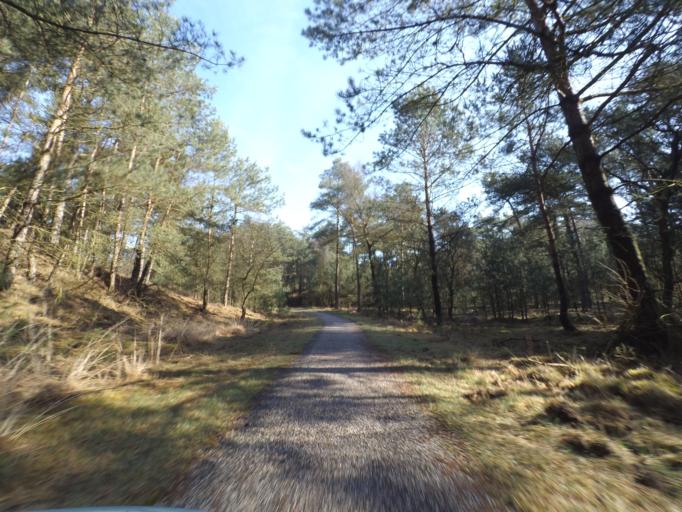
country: NL
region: Gelderland
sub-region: Gemeente Ede
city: Harskamp
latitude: 52.1644
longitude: 5.7388
